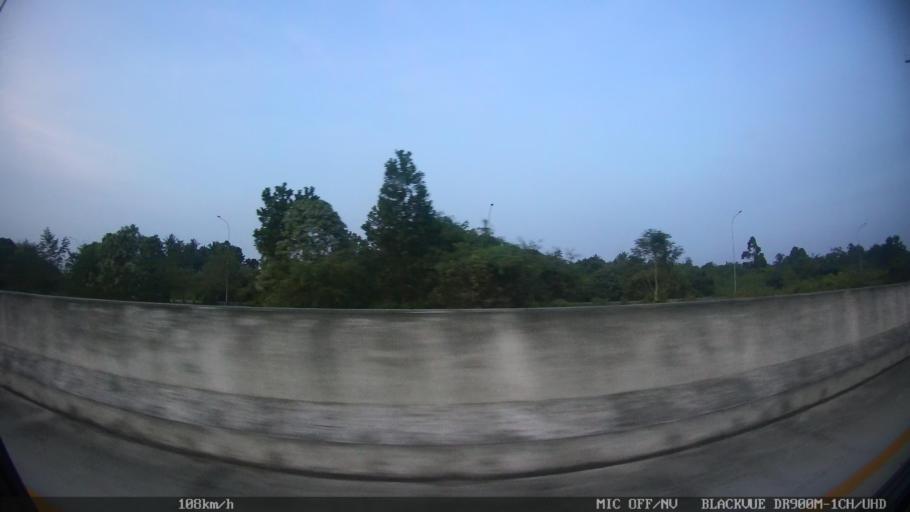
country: ID
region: Lampung
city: Kalianda
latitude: -5.6942
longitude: 105.6241
